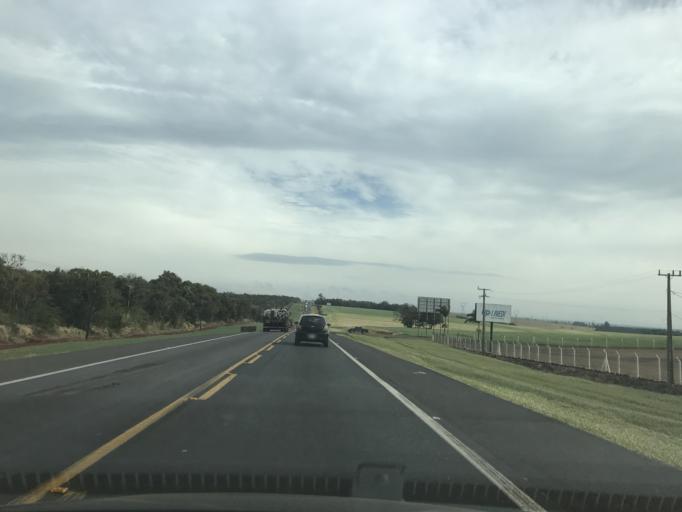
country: BR
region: Parana
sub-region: Cascavel
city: Cascavel
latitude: -25.0779
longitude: -53.6980
